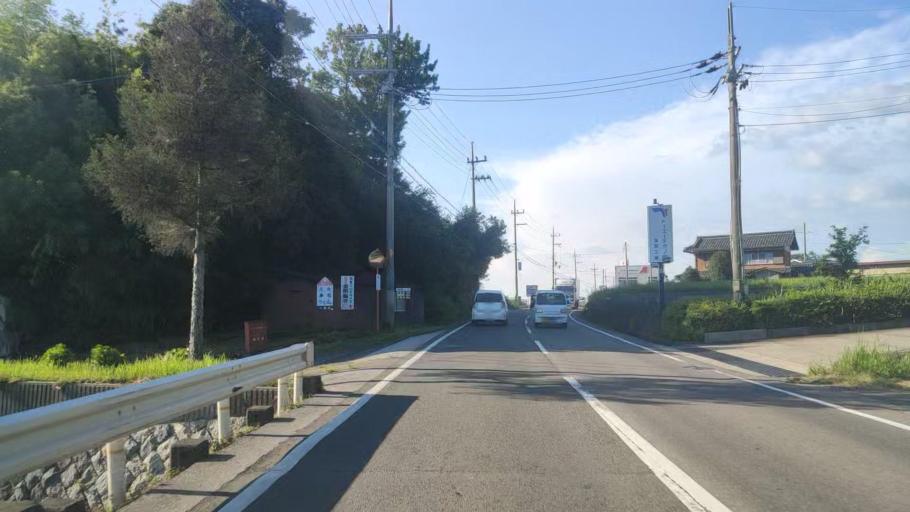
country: JP
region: Shiga Prefecture
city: Youkaichi
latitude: 35.1208
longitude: 136.2565
